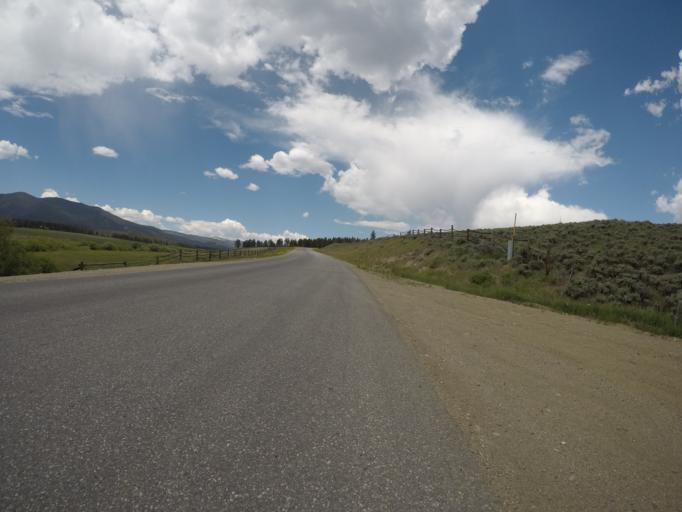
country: US
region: Colorado
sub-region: Grand County
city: Fraser
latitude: 39.9838
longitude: -105.8733
